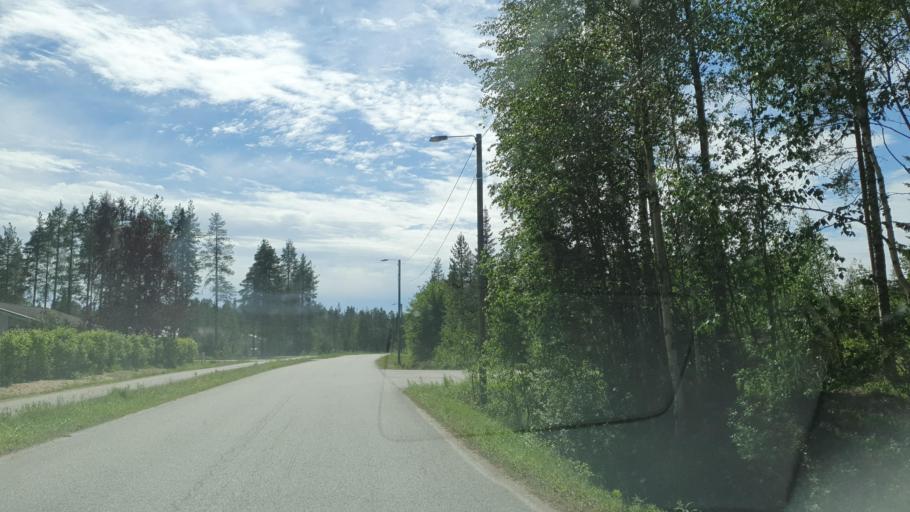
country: FI
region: Kainuu
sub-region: Kehys-Kainuu
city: Hyrynsalmi
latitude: 64.6890
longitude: 28.4693
